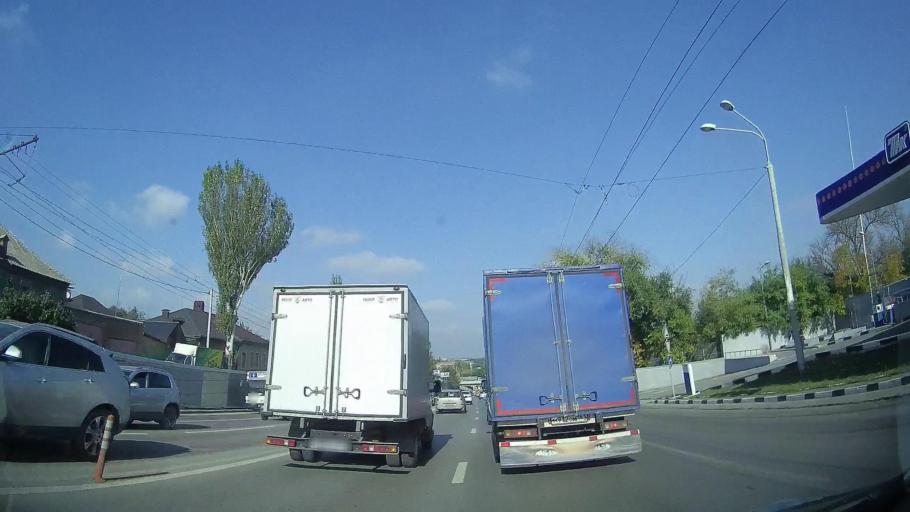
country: RU
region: Rostov
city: Rostov-na-Donu
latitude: 47.2419
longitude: 39.6979
